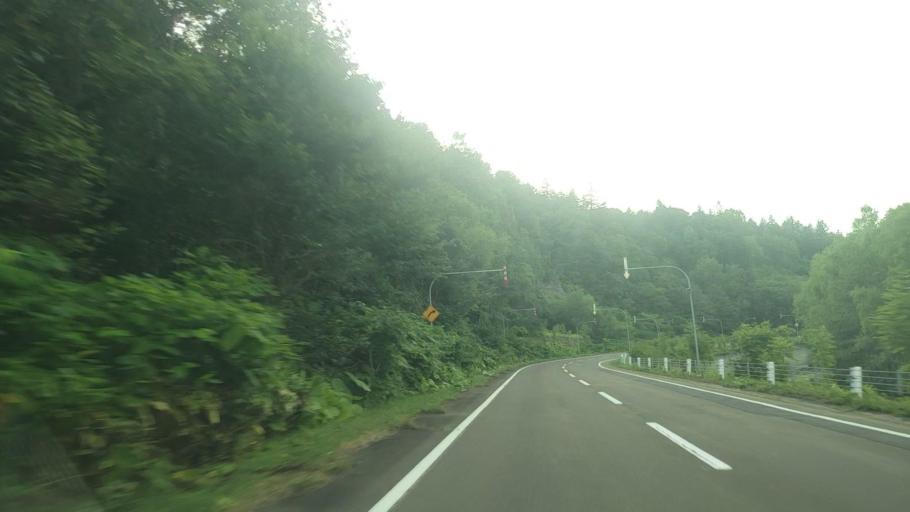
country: JP
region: Hokkaido
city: Bibai
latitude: 43.1297
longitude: 142.0958
